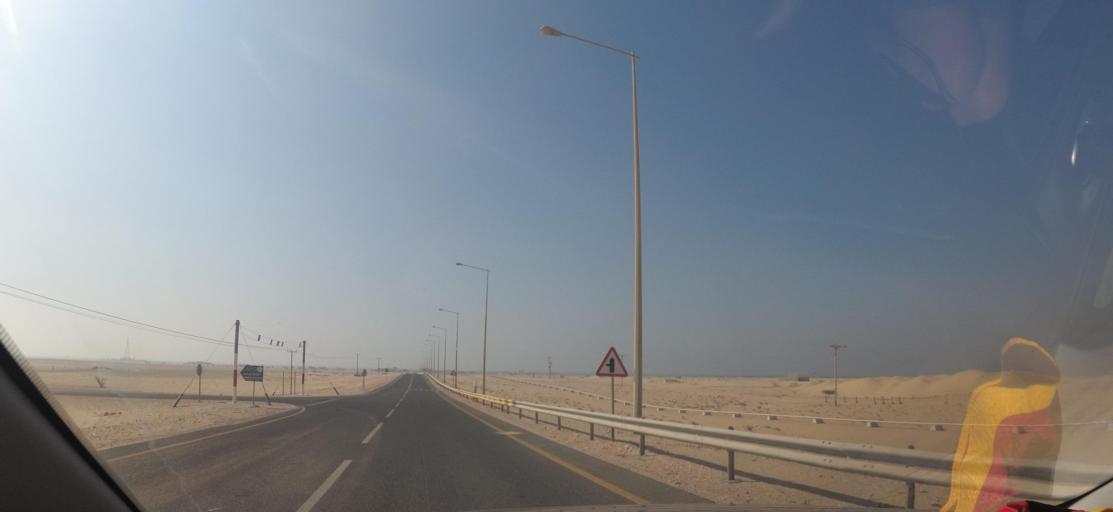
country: QA
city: Umm Bab
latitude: 25.2116
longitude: 50.7825
